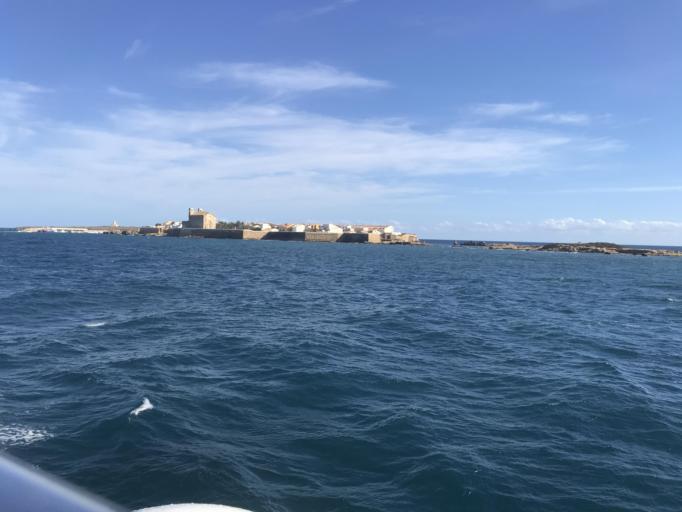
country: ES
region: Valencia
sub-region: Provincia de Alicante
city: Santa Pola
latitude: 38.1699
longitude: -0.4877
